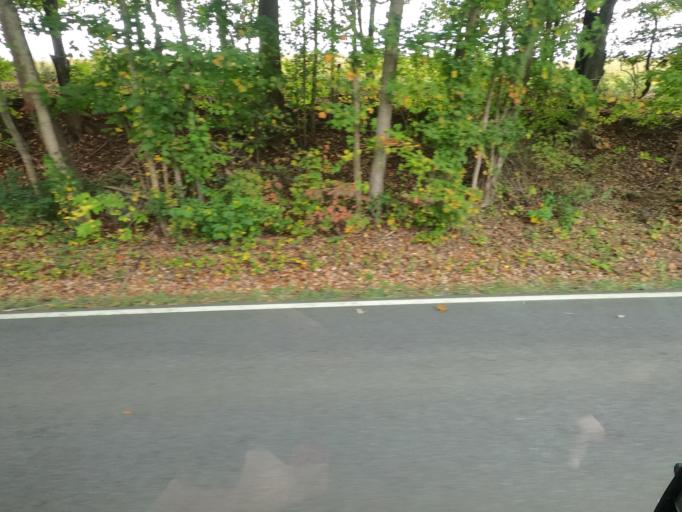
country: US
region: Tennessee
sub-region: Washington County
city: Jonesborough
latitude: 36.2458
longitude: -82.5501
